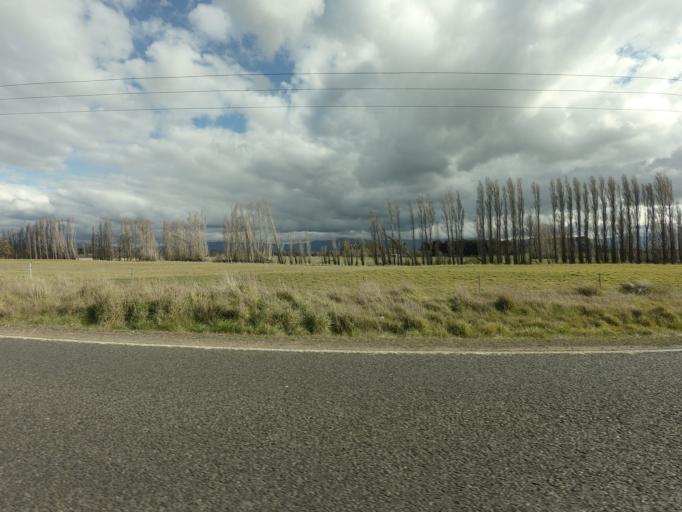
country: AU
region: Tasmania
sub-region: Northern Midlands
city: Longford
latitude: -41.7159
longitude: 147.0877
